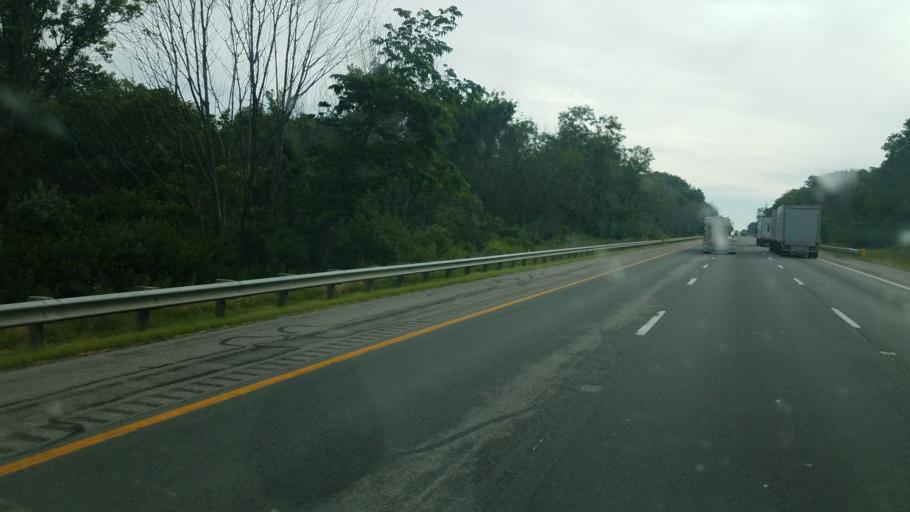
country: US
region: Ohio
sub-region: Ashland County
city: Ashland
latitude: 40.8088
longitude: -82.3693
